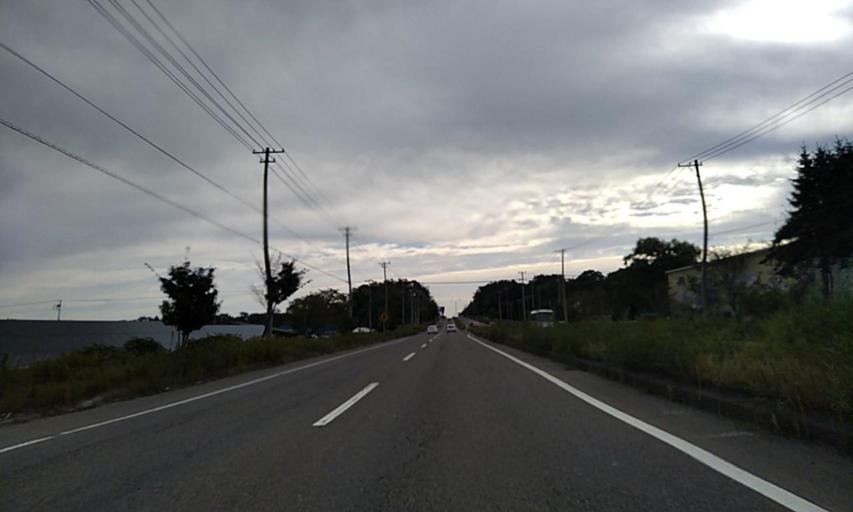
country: JP
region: Hokkaido
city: Obihiro
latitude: 42.9205
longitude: 143.0396
